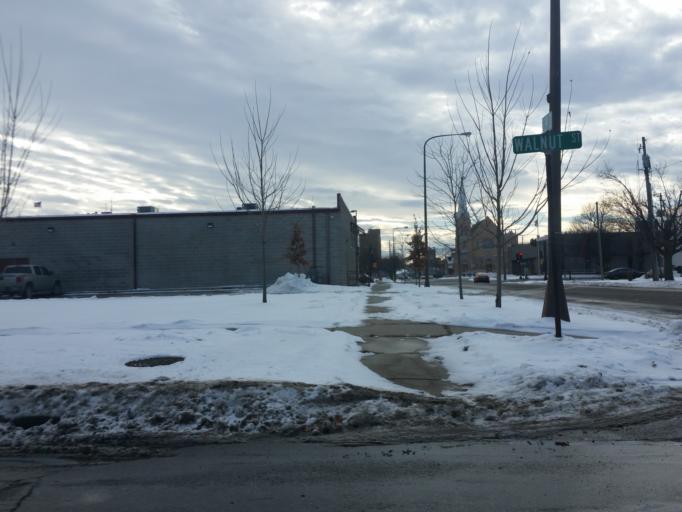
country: US
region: Iowa
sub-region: Black Hawk County
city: Waterloo
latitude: 42.5027
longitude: -92.3343
